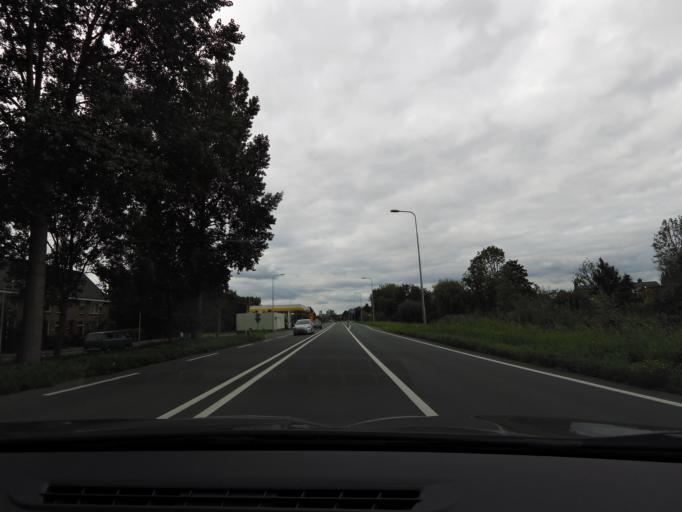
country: NL
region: South Holland
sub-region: Gemeente Krimpen aan den IJssel
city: Krimpen aan den IJssel
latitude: 51.9089
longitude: 4.5939
